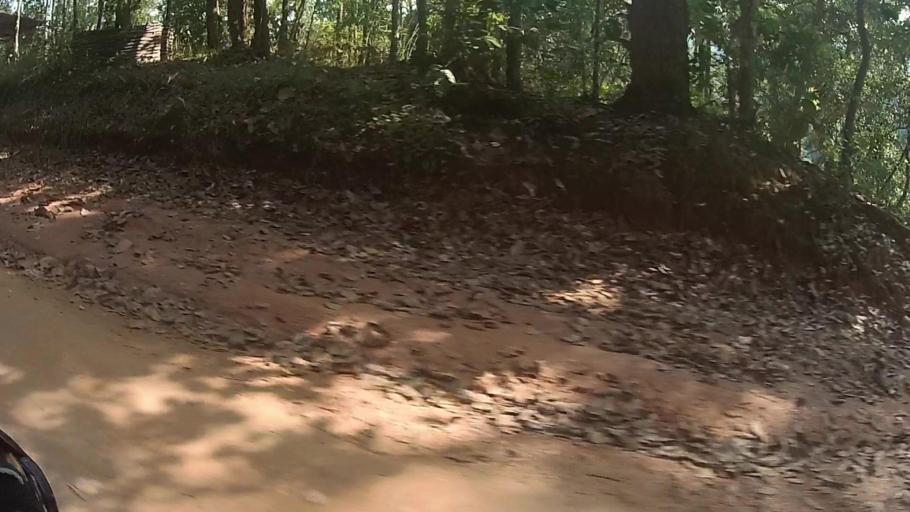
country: TH
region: Chiang Mai
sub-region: Amphoe Chiang Dao
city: Chiang Dao
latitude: 19.3353
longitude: 98.9010
